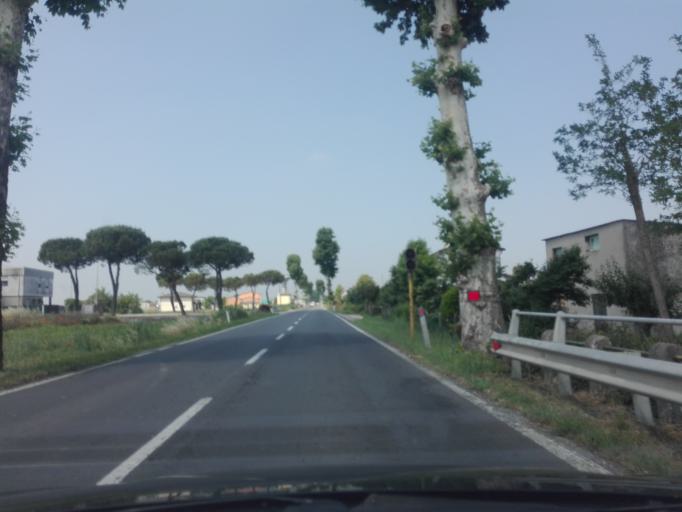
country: IT
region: Veneto
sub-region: Provincia di Rovigo
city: Villadose
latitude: 45.0650
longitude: 11.9111
